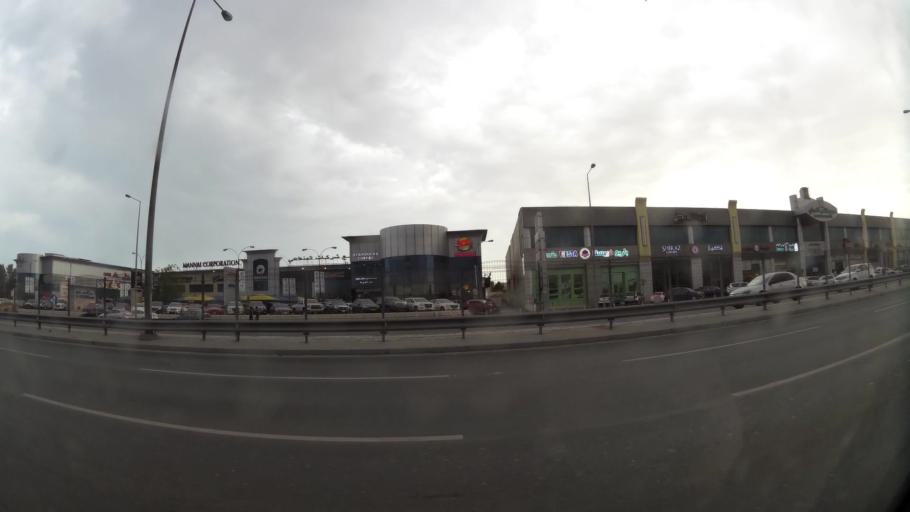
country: QA
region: Baladiyat ad Dawhah
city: Doha
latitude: 25.2712
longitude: 51.5086
